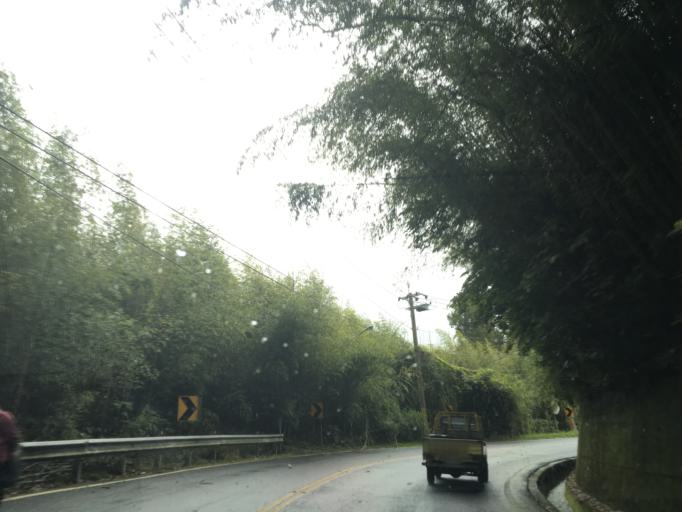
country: TW
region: Taiwan
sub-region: Chiayi
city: Jiayi Shi
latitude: 23.4474
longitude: 120.6774
